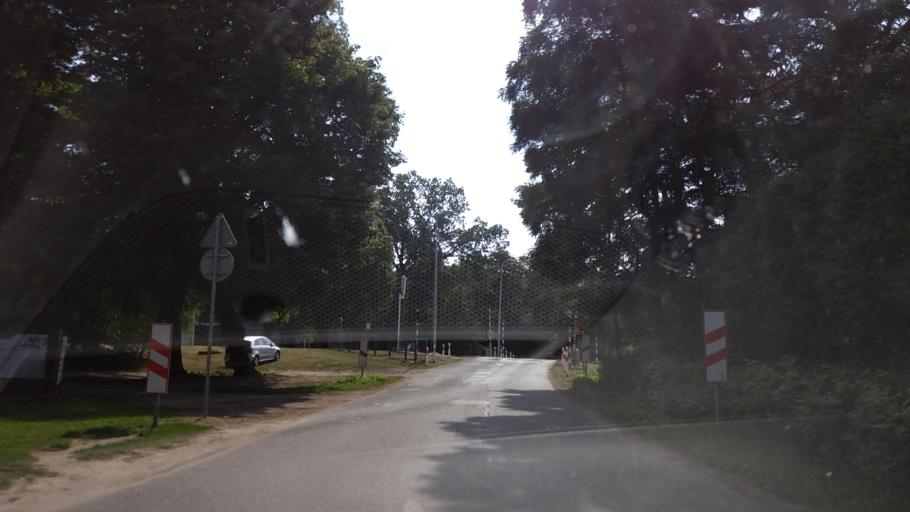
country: PL
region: West Pomeranian Voivodeship
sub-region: Powiat stargardzki
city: Stargard Szczecinski
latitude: 53.3588
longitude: 14.9725
